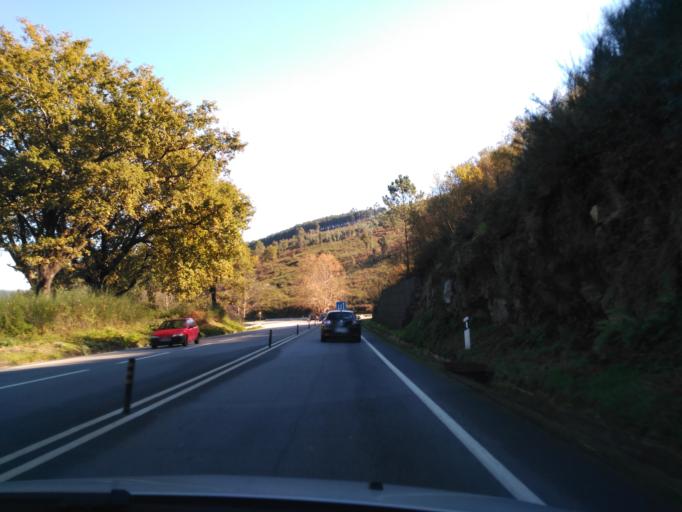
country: PT
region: Braga
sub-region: Povoa de Lanhoso
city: Povoa de Lanhoso
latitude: 41.5846
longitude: -8.3078
